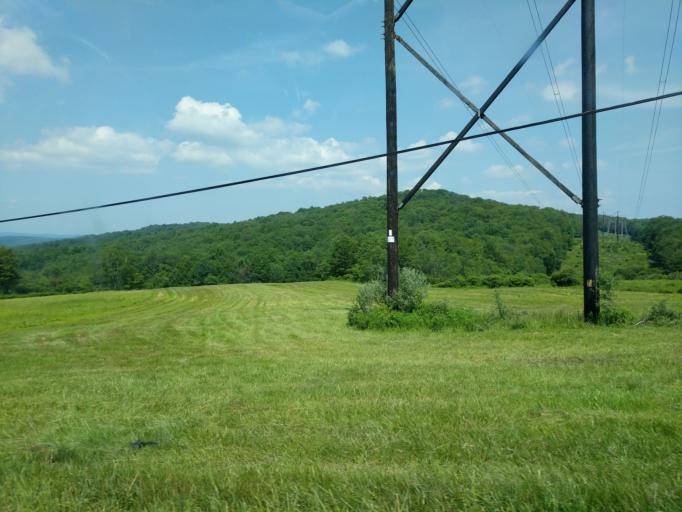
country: US
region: New York
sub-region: Sullivan County
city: Livingston Manor
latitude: 41.9022
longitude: -74.9454
